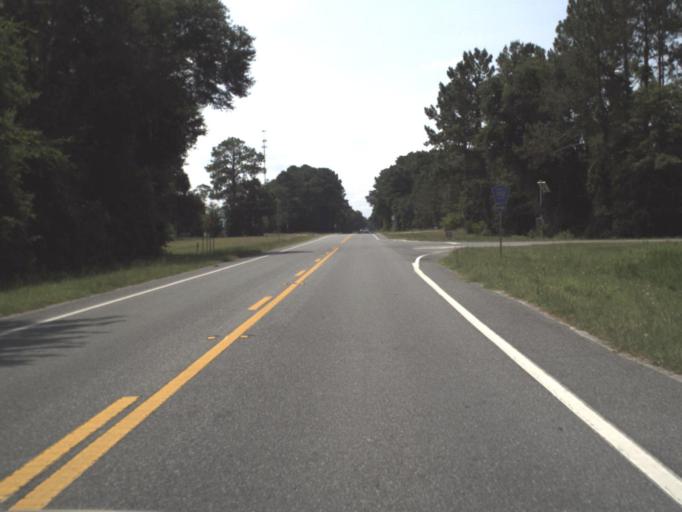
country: US
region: Florida
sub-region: Hamilton County
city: Jasper
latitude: 30.5527
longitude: -83.0625
